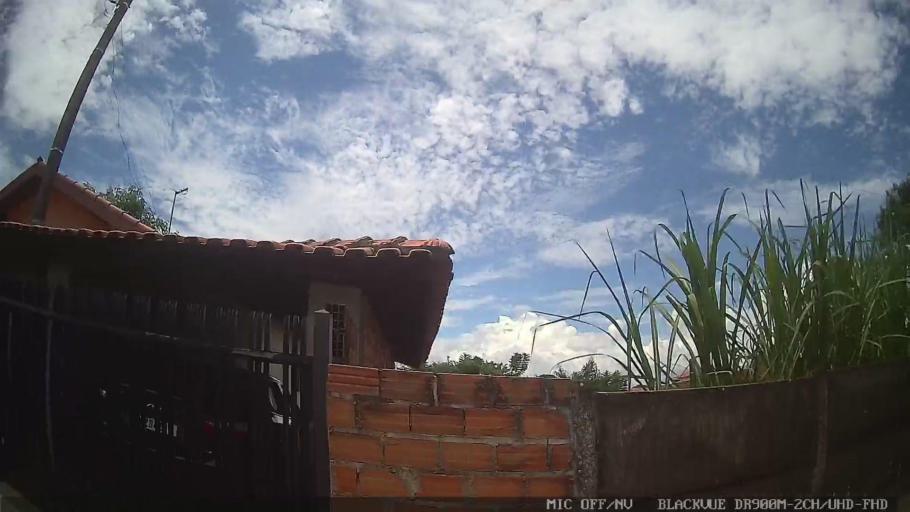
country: BR
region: Sao Paulo
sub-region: Conchas
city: Conchas
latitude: -23.0704
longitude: -47.9785
